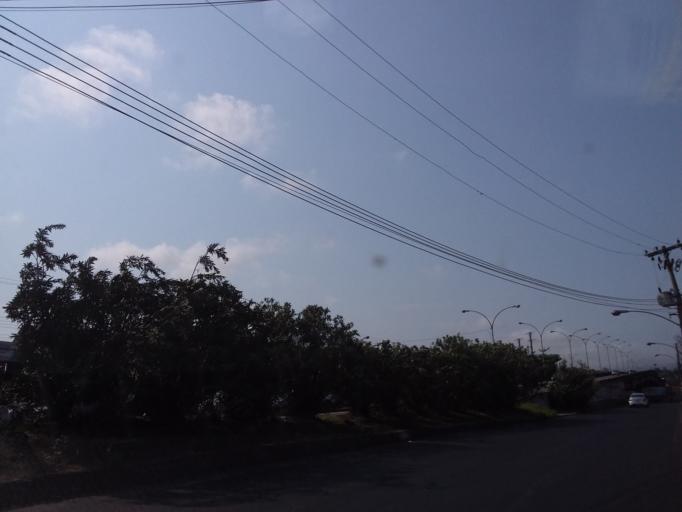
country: BR
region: Rio de Janeiro
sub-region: Nilopolis
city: Nilopolis
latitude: -22.9023
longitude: -43.5503
